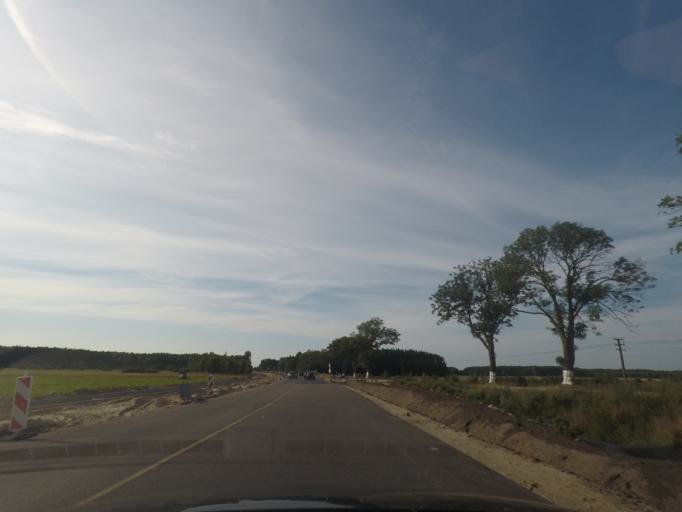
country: PL
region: Pomeranian Voivodeship
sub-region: Powiat leborski
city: Leba
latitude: 54.7283
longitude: 17.5681
